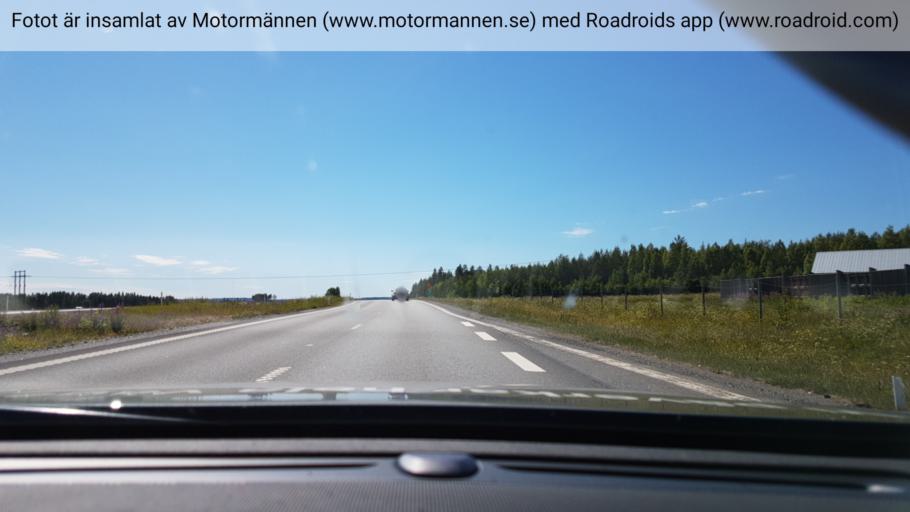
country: SE
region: Vaesterbotten
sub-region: Skelleftea Kommun
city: Kage
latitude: 64.8837
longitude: 21.0429
